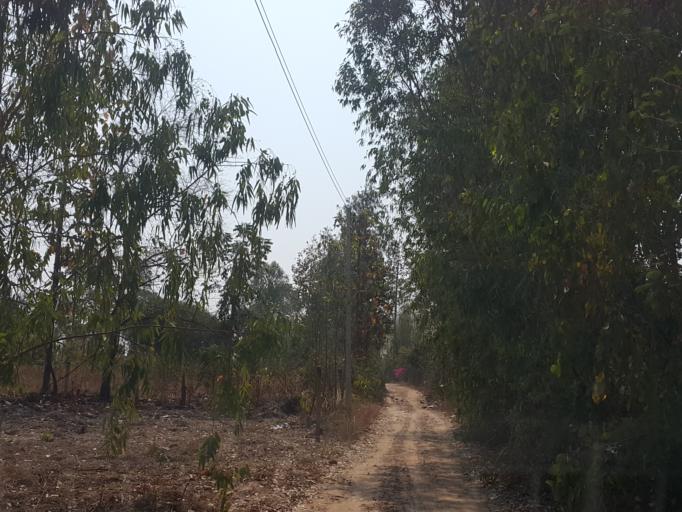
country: TH
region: Chiang Mai
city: Hang Dong
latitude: 18.6865
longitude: 98.8756
